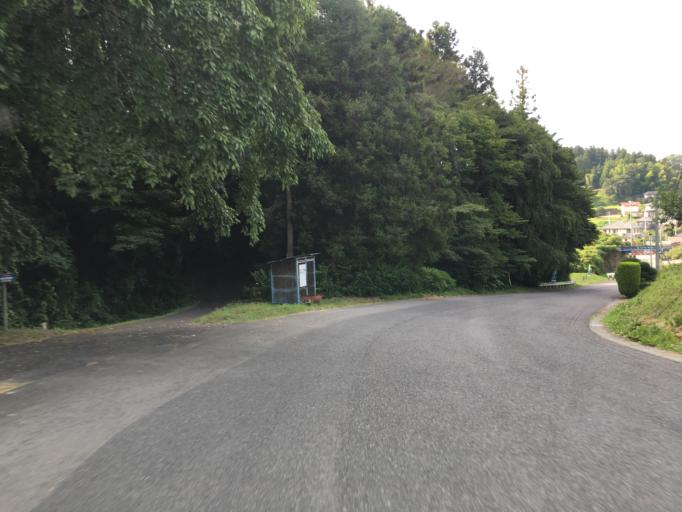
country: JP
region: Fukushima
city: Miharu
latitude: 37.4184
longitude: 140.4427
